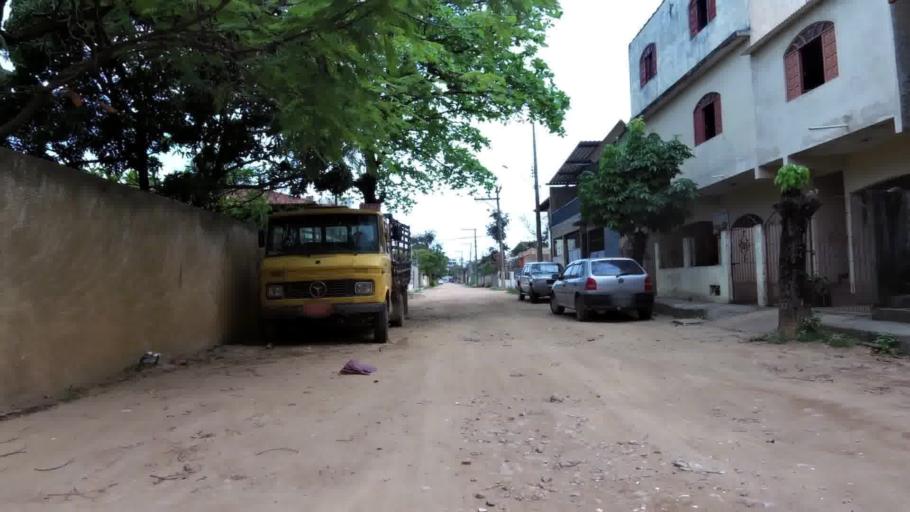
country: BR
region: Espirito Santo
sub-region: Piuma
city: Piuma
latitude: -20.8399
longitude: -40.7315
